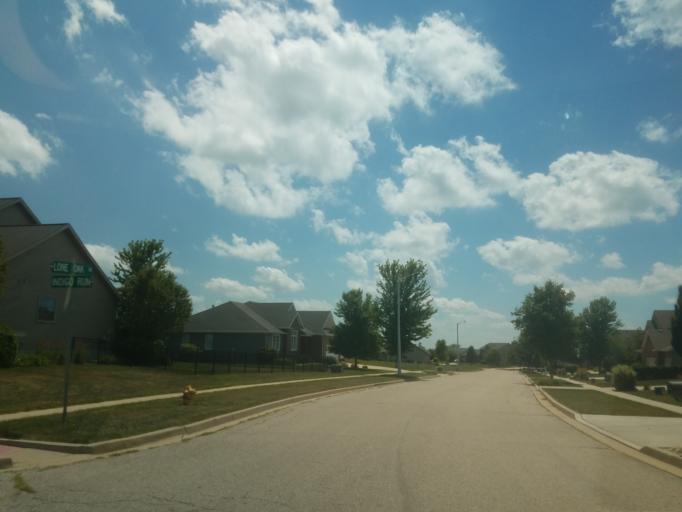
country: US
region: Illinois
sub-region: McLean County
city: Bloomington
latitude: 40.4452
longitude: -89.0342
